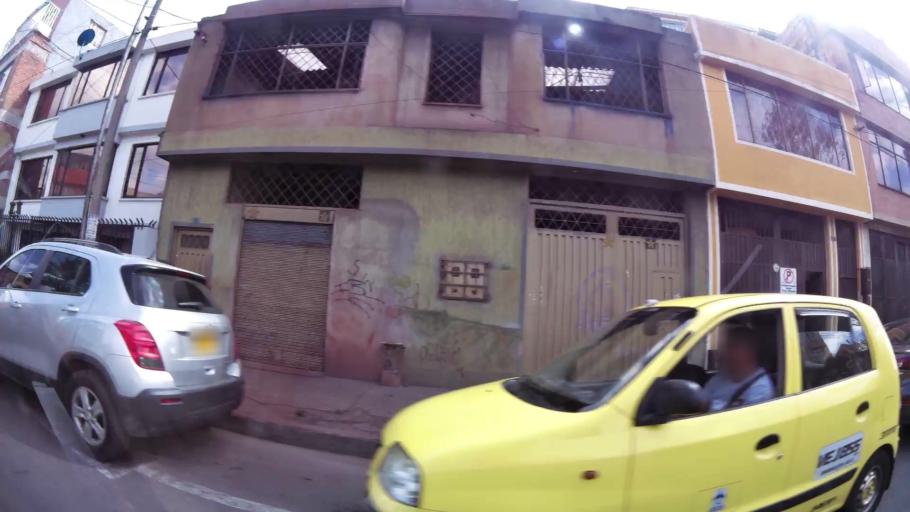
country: CO
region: Bogota D.C.
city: Bogota
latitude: 4.6121
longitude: -74.1327
